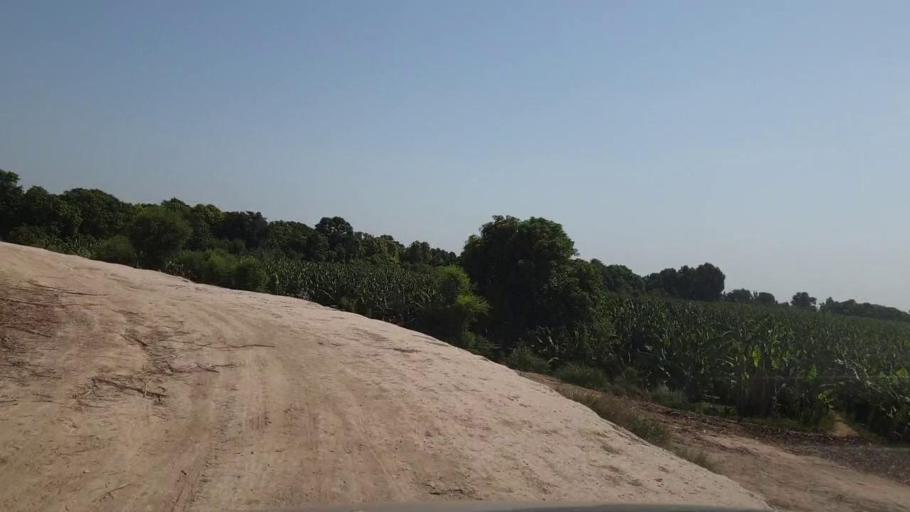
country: PK
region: Sindh
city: Matiari
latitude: 25.6272
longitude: 68.4780
